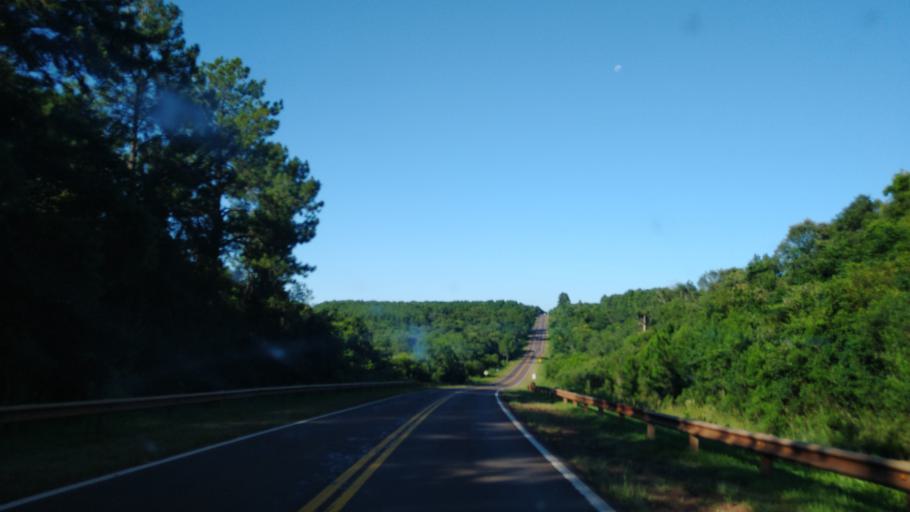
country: AR
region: Misiones
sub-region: Departamento de San Ignacio
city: San Ignacio
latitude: -27.2330
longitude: -55.5157
